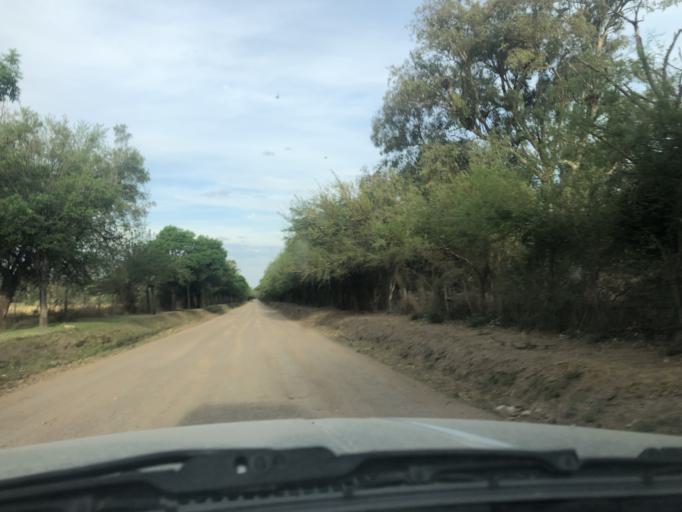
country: AR
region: Cordoba
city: La Granja
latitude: -31.0175
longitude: -64.2499
